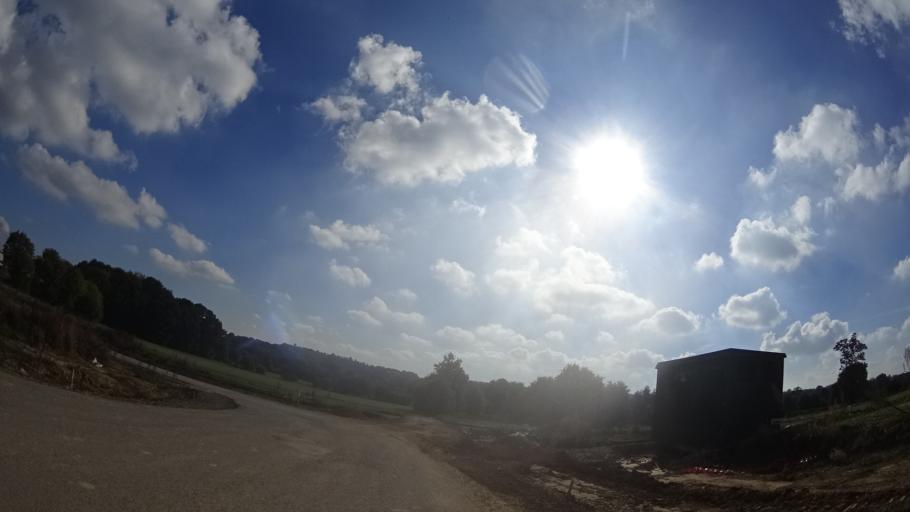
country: FR
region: Brittany
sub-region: Departement d'Ille-et-Vilaine
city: Geveze
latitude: 48.2200
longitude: -1.8015
